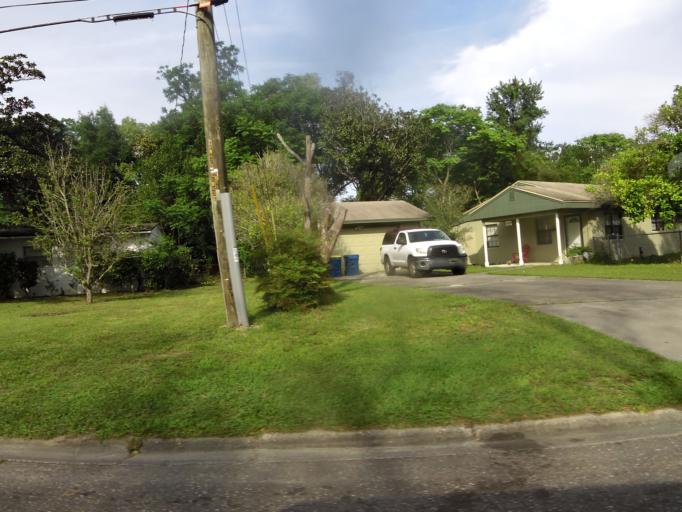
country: US
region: Florida
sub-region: Duval County
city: Jacksonville
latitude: 30.3392
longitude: -81.5871
